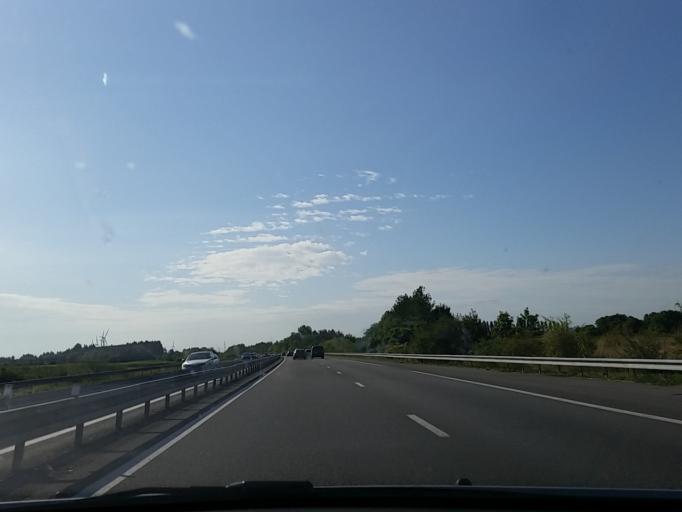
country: FR
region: Centre
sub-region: Departement du Cher
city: Mehun-sur-Yevre
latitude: 47.1232
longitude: 2.1919
